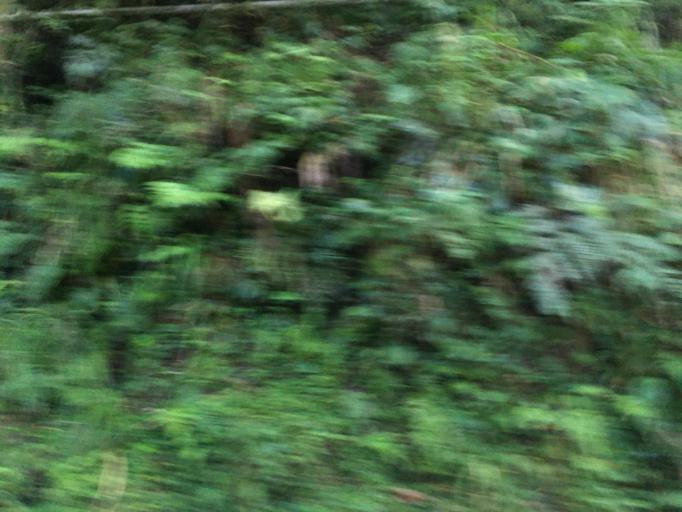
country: TW
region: Taiwan
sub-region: Yilan
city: Yilan
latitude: 24.6210
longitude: 121.4799
